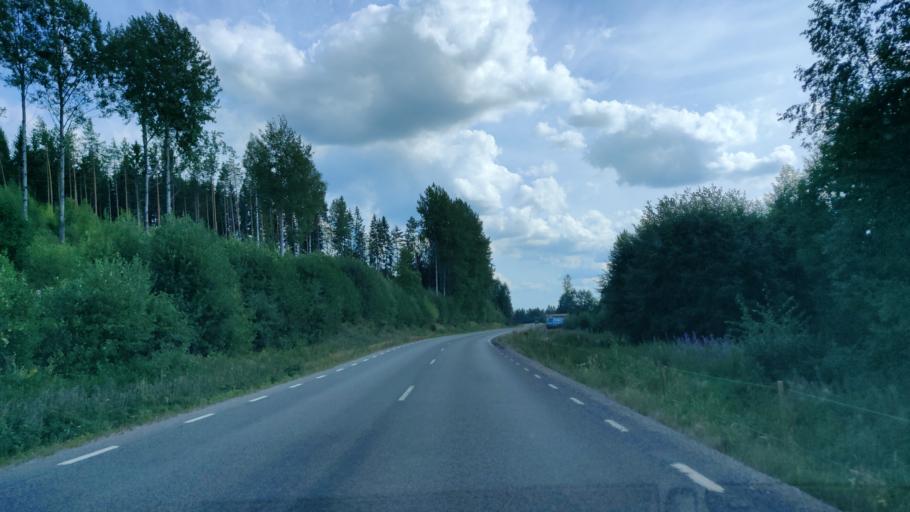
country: SE
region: Vaermland
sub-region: Hagfors Kommun
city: Ekshaerad
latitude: 60.1664
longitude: 13.5311
